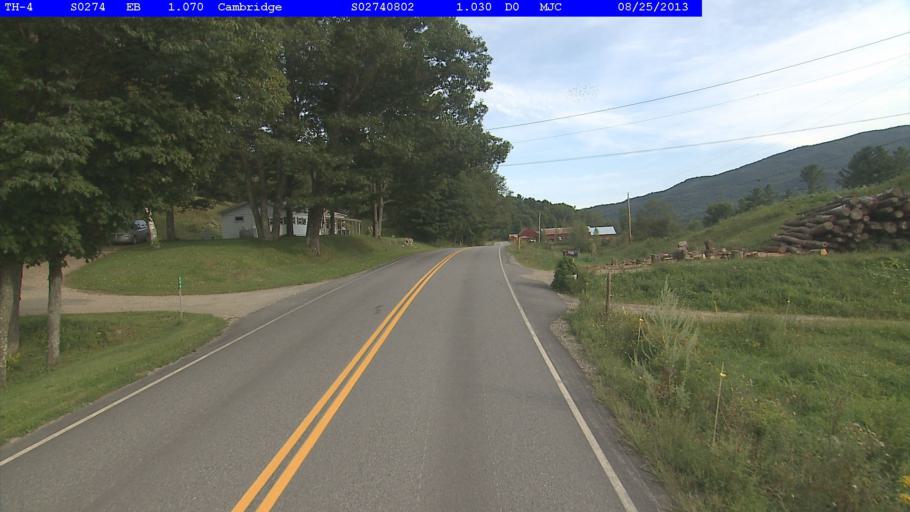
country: US
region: Vermont
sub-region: Lamoille County
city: Johnson
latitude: 44.6695
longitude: -72.7634
